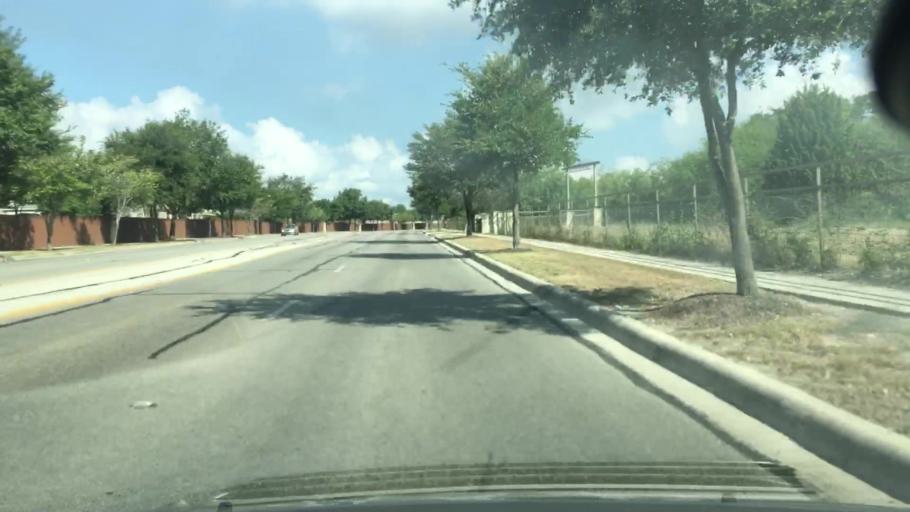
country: US
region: Texas
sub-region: Guadalupe County
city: Cibolo
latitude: 29.5795
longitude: -98.2454
